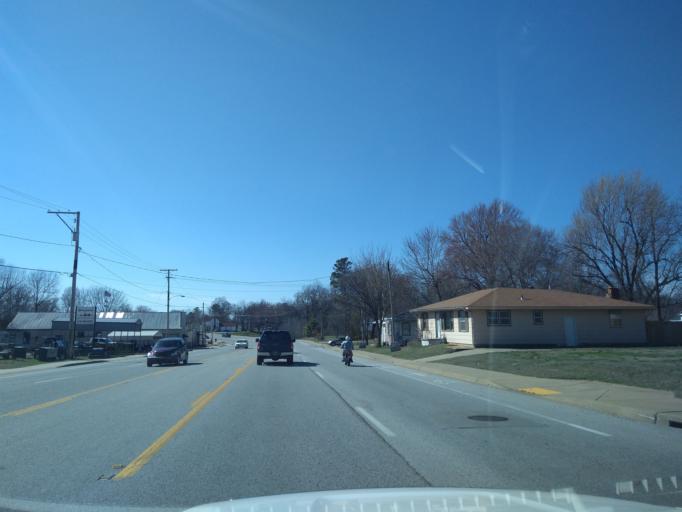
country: US
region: Arkansas
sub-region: Washington County
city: Farmington
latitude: 36.0420
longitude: -94.2459
